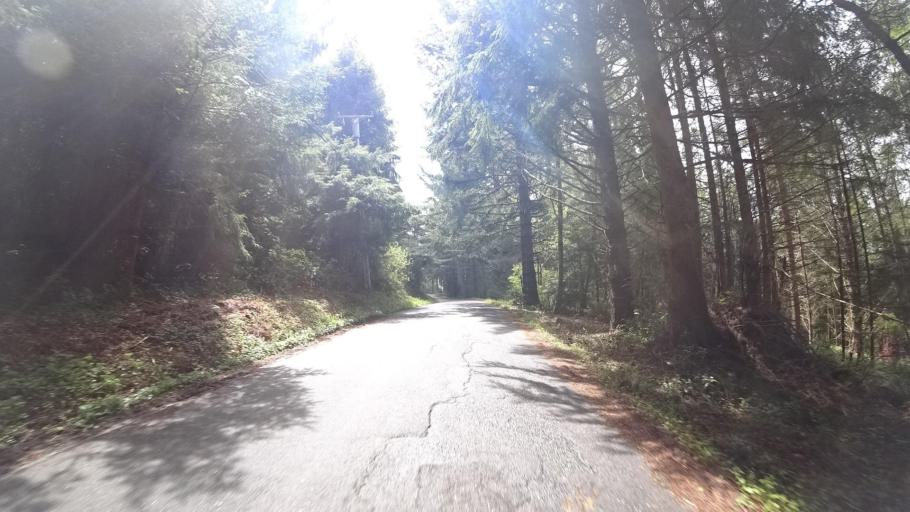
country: US
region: California
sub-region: Humboldt County
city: Bayside
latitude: 40.8325
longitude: -124.0131
